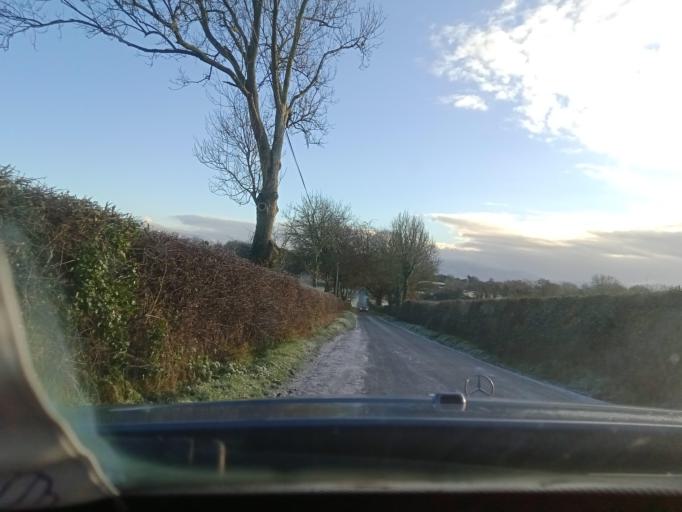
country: IE
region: Leinster
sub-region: Kilkenny
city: Graiguenamanagh
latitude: 52.5990
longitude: -6.9729
